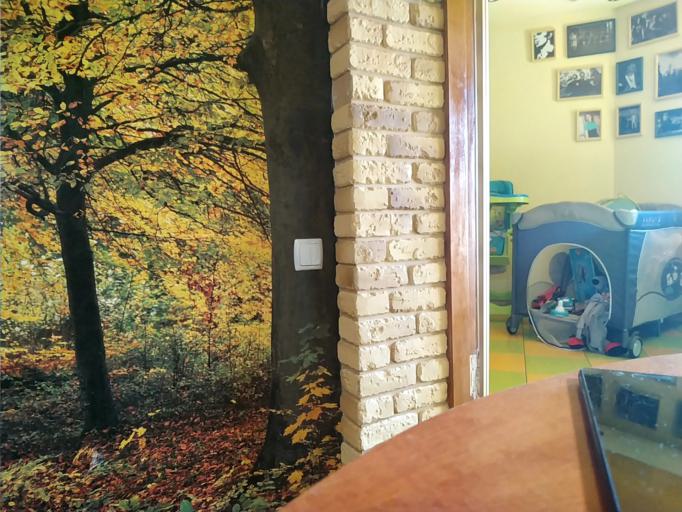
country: RU
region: Tverskaya
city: Krasnomayskiy
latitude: 57.6230
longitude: 34.4166
